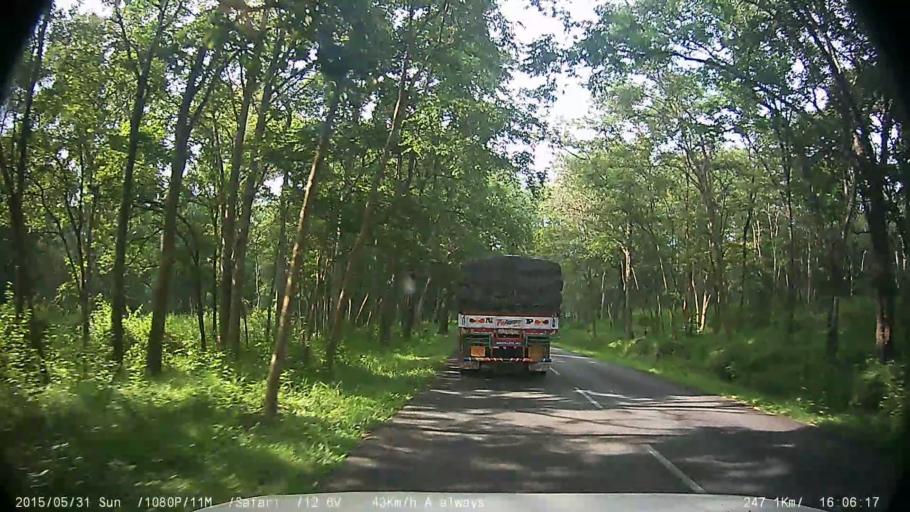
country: IN
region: Tamil Nadu
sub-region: Nilgiri
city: Masinigudi
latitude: 11.7173
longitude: 76.4236
